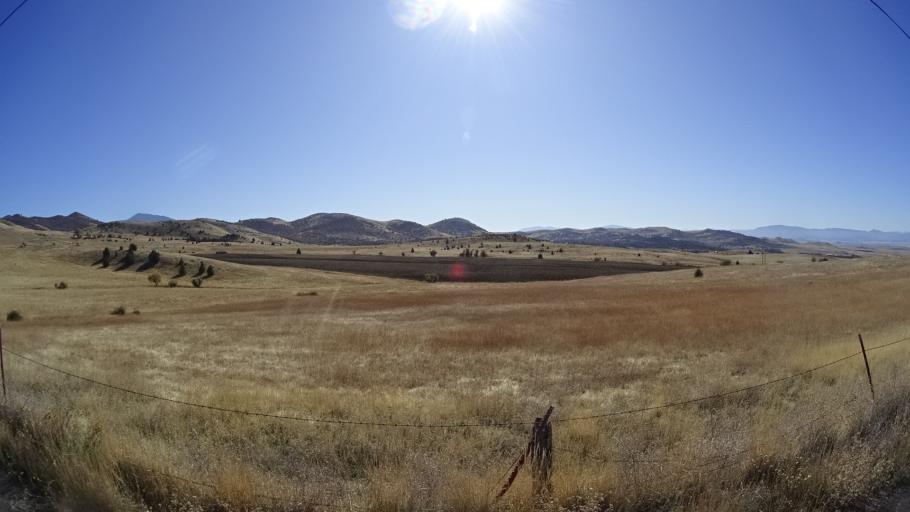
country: US
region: California
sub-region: Siskiyou County
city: Montague
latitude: 41.8300
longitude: -122.3590
